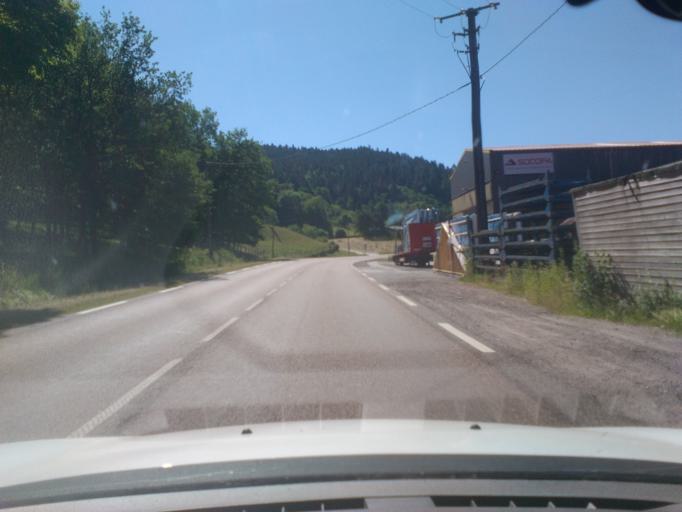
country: FR
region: Lorraine
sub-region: Departement des Vosges
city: Vagney
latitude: 47.9809
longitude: 6.7255
